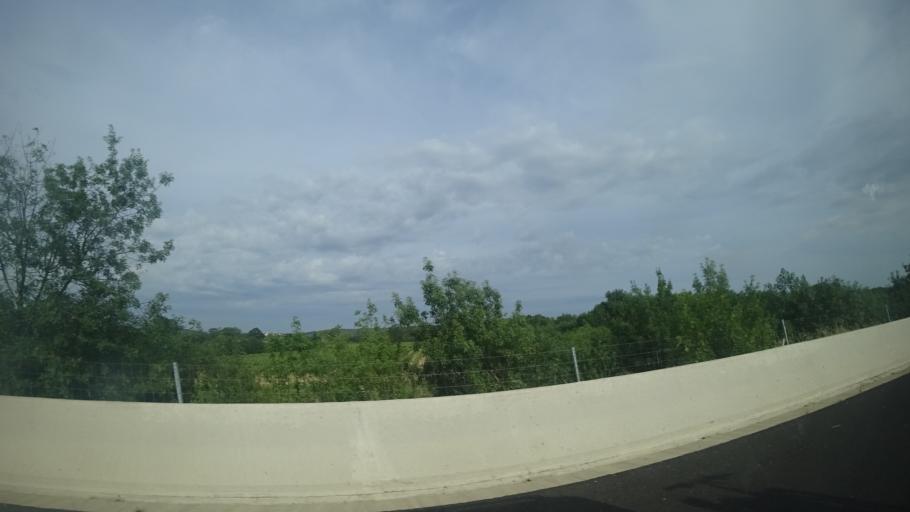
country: FR
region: Languedoc-Roussillon
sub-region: Departement de l'Herault
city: Pezenas
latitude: 43.4665
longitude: 3.4330
